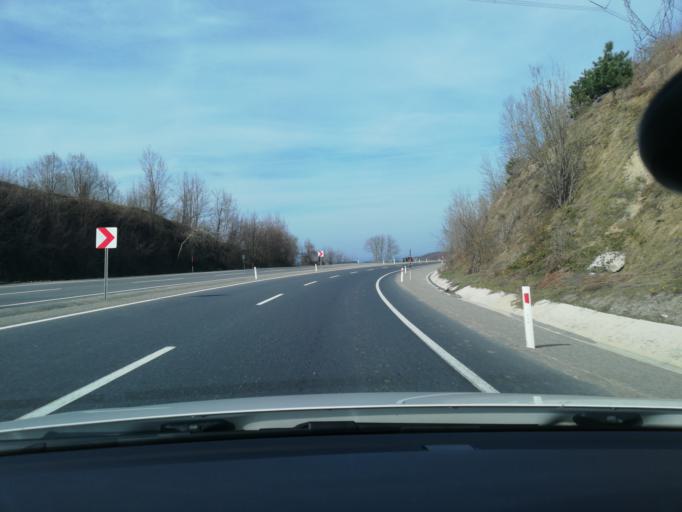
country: TR
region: Zonguldak
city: Kozlu
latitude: 41.3406
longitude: 31.6292
